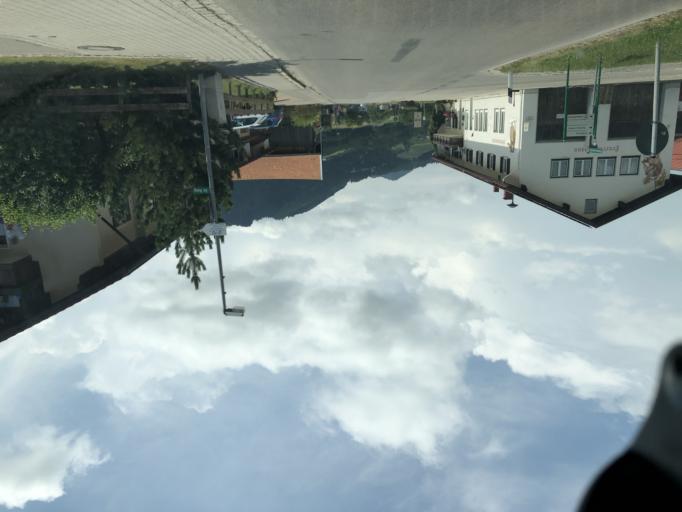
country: DE
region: Bavaria
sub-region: Swabia
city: Wertach
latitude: 47.6022
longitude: 10.4146
